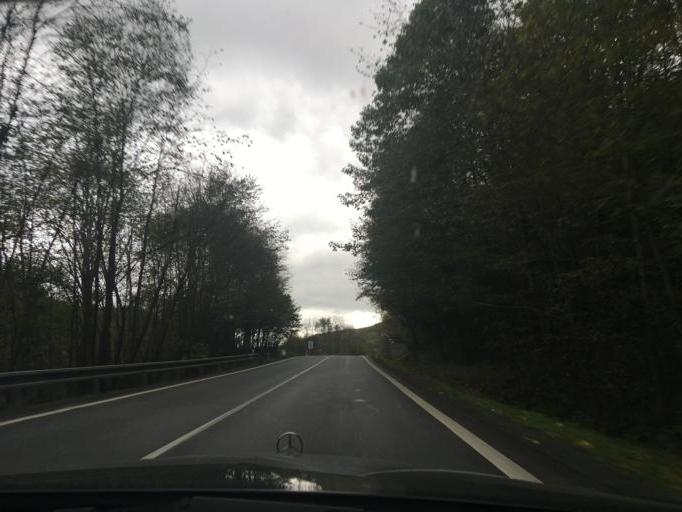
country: SK
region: Presovsky
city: Svidnik
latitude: 49.3671
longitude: 21.6901
